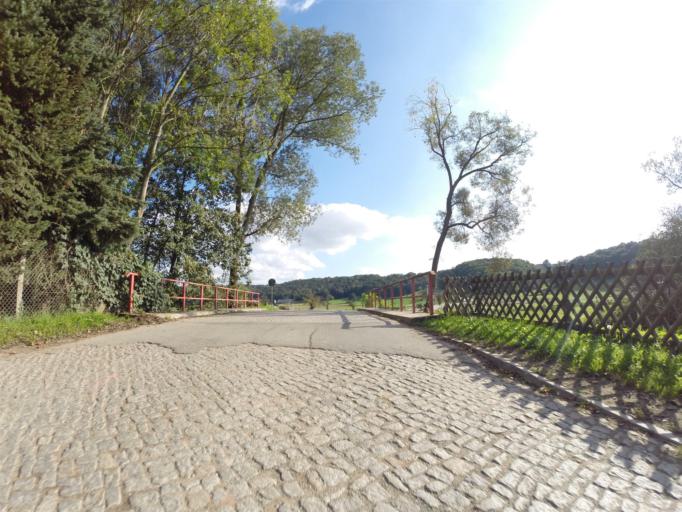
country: DE
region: Thuringia
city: Sulza
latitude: 50.8731
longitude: 11.6222
